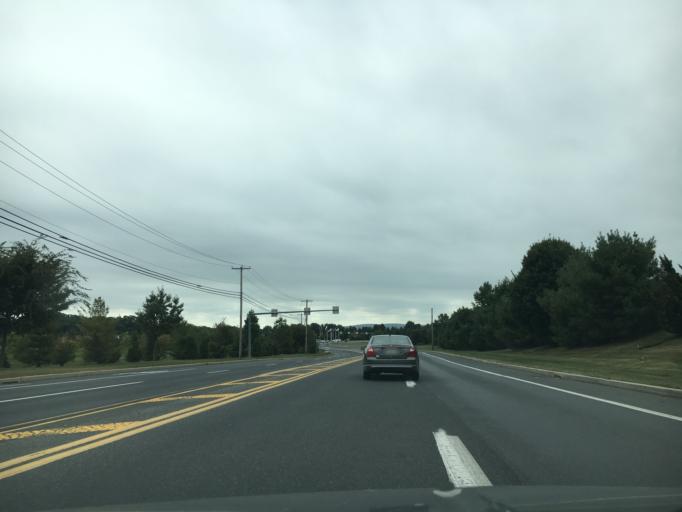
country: US
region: Pennsylvania
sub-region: Northampton County
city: Bath
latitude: 40.6853
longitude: -75.3910
